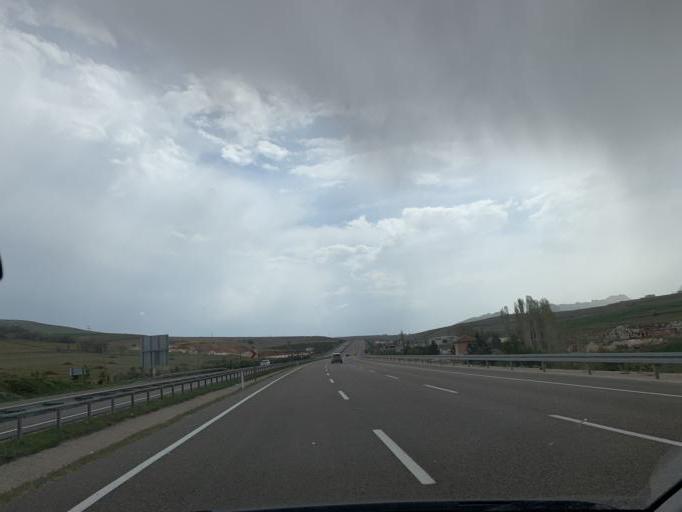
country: TR
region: Eskisehir
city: Sivrihisar
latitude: 39.4838
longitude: 31.5980
